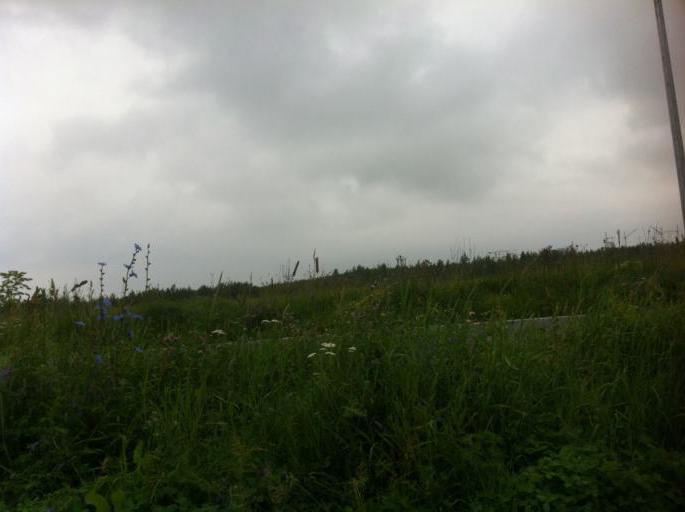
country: RU
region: St.-Petersburg
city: Sosnovaya Polyana
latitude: 59.8554
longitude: 30.1499
